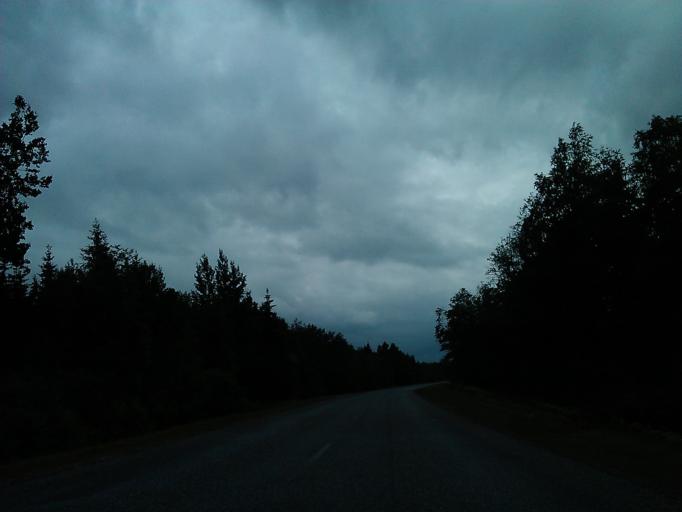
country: LV
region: Kuldigas Rajons
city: Kuldiga
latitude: 56.9870
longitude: 22.0744
